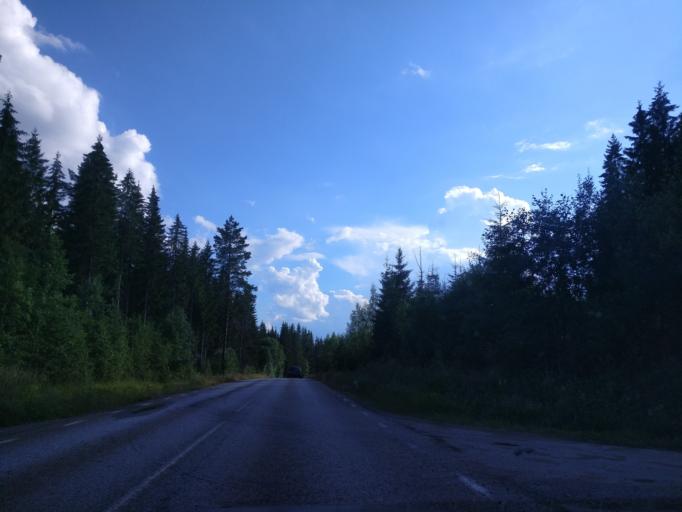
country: SE
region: Dalarna
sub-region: Ludvika Kommun
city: Ludvika
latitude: 60.2736
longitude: 15.0733
